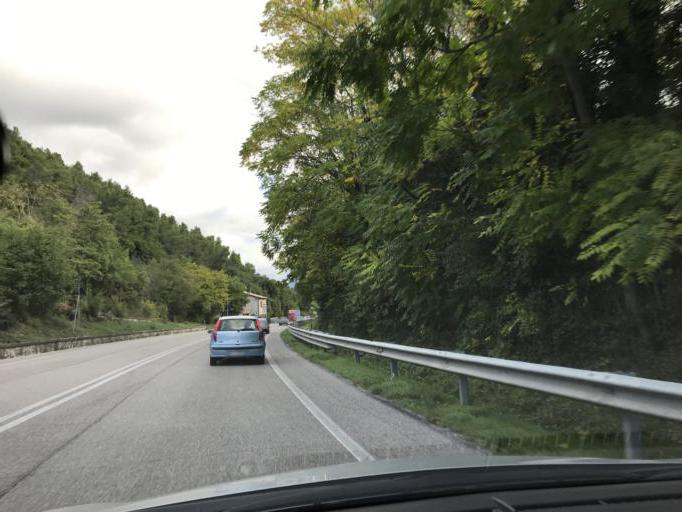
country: IT
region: Umbria
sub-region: Provincia di Perugia
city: Spoleto
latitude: 42.7125
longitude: 12.7202
